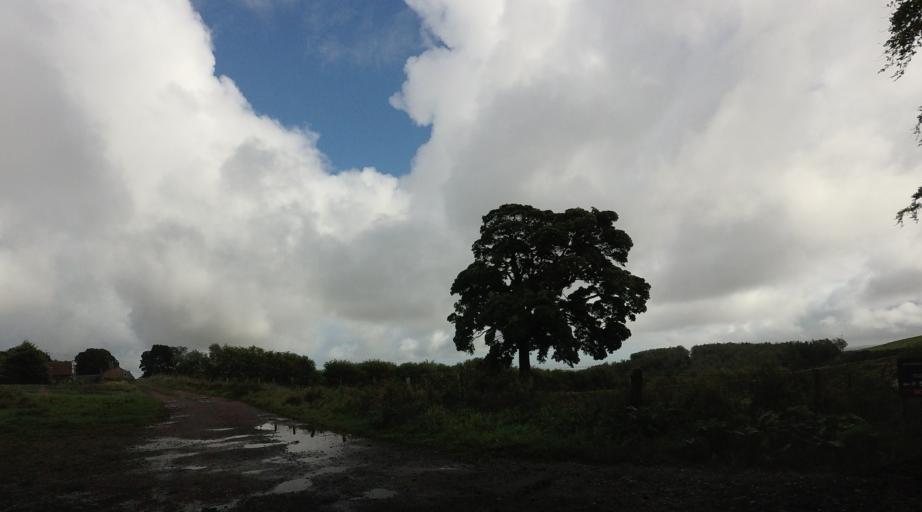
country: GB
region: Scotland
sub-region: Fife
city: Balmullo
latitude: 56.3756
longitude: -2.9564
